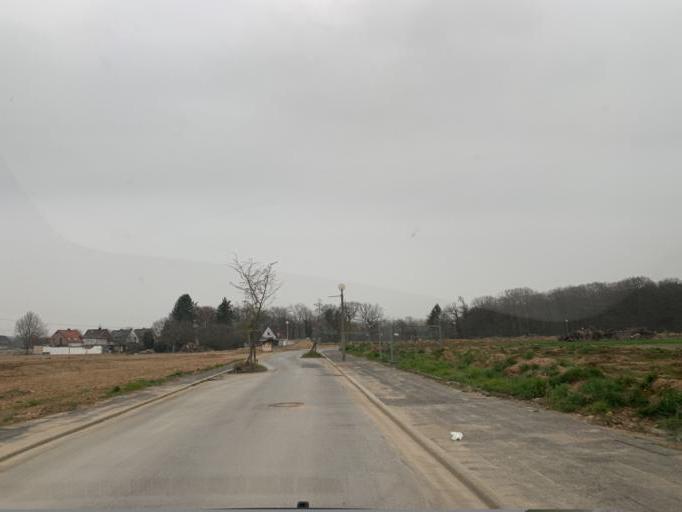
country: DE
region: North Rhine-Westphalia
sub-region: Regierungsbezirk Koln
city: Elsdorf
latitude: 50.8846
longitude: 6.5976
